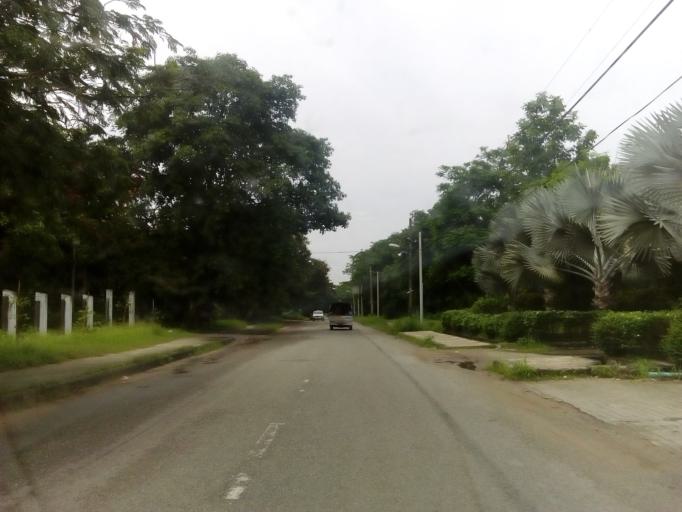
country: MM
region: Yangon
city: Yangon
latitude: 16.8546
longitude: 96.1299
